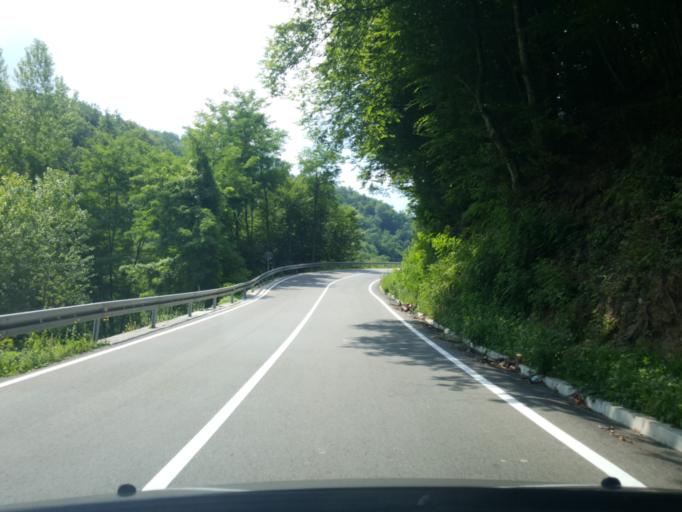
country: RS
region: Central Serbia
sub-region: Moravicki Okrug
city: Gornji Milanovac
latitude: 44.1646
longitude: 20.5140
